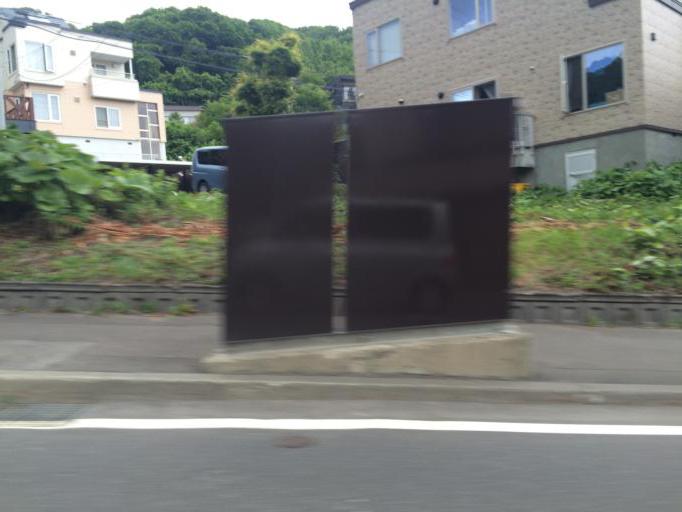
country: JP
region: Hokkaido
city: Sapporo
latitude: 43.0422
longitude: 141.2912
